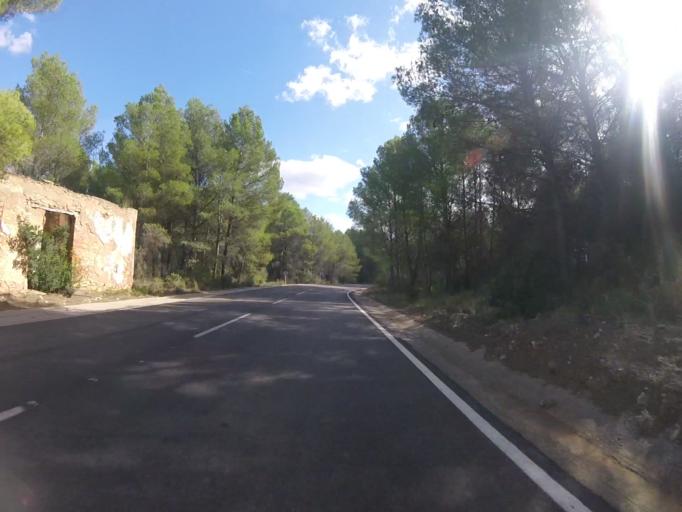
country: ES
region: Valencia
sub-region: Provincia de Castello
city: Cuevas de Vinroma
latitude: 40.3041
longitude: 0.1641
